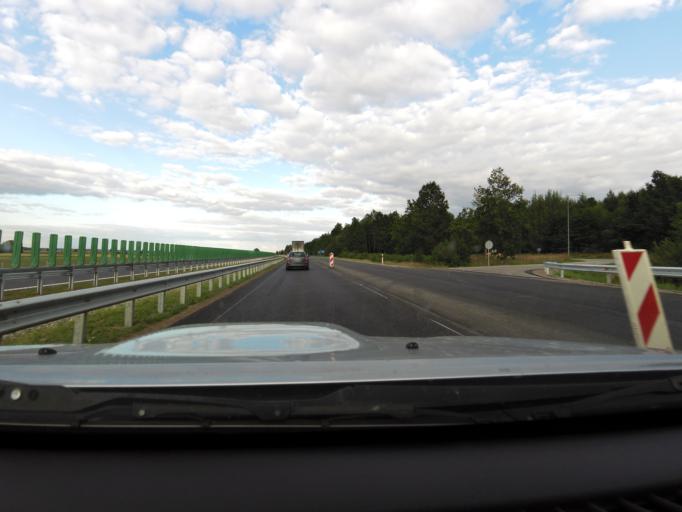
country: LT
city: Kazlu Ruda
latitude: 54.6760
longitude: 23.5631
